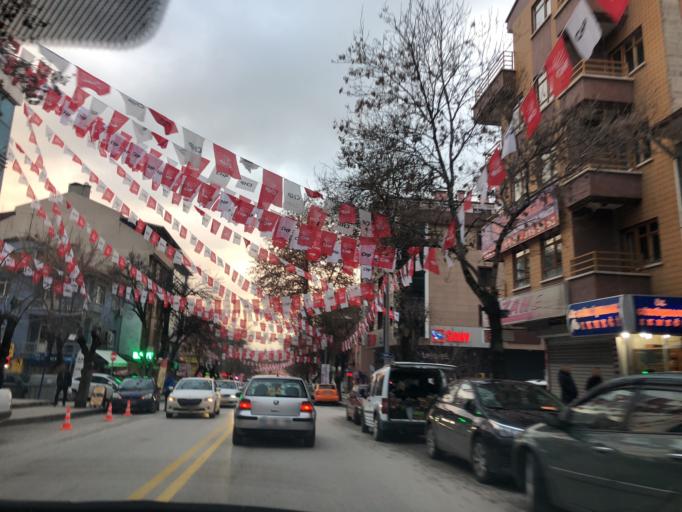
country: TR
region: Ankara
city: Ankara
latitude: 39.9655
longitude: 32.8086
